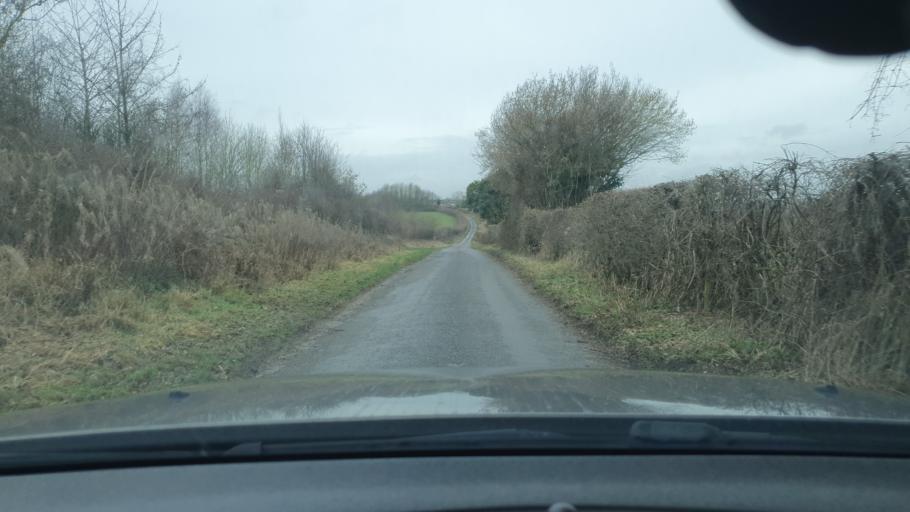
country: GB
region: England
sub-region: West Berkshire
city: Kintbury
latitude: 51.3967
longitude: -1.4274
